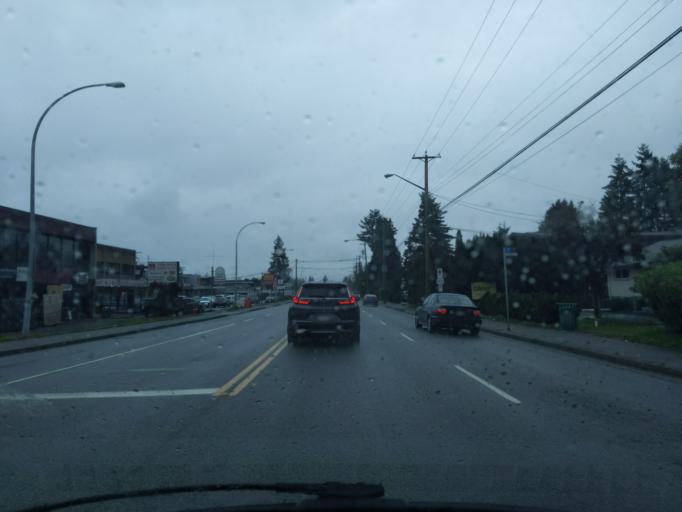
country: CA
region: British Columbia
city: Port Moody
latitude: 49.1987
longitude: -122.8174
